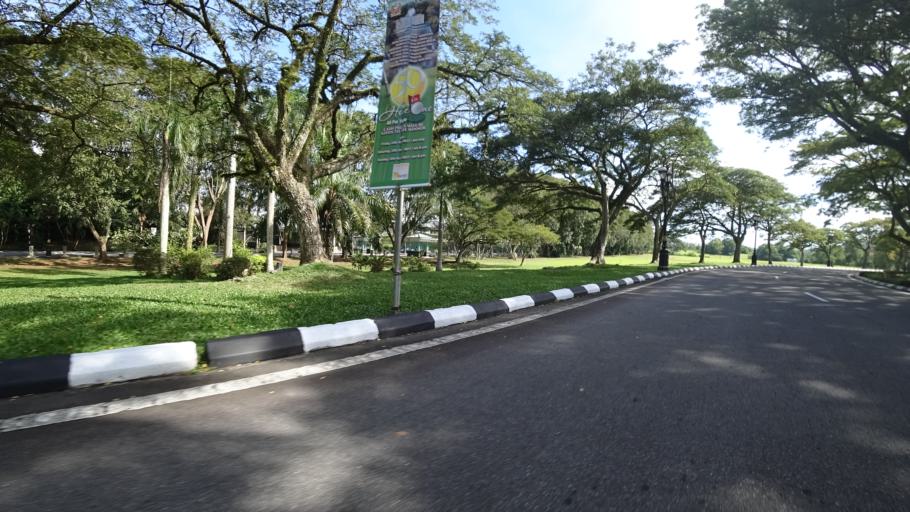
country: BN
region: Brunei and Muara
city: Bandar Seri Begawan
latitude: 4.9448
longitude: 114.8331
